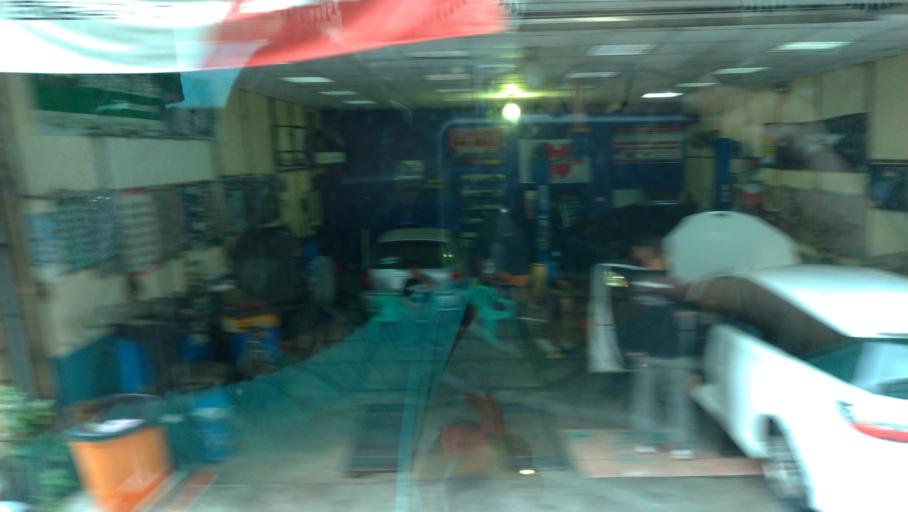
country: TW
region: Taiwan
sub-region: Keelung
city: Keelung
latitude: 25.1450
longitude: 121.7616
